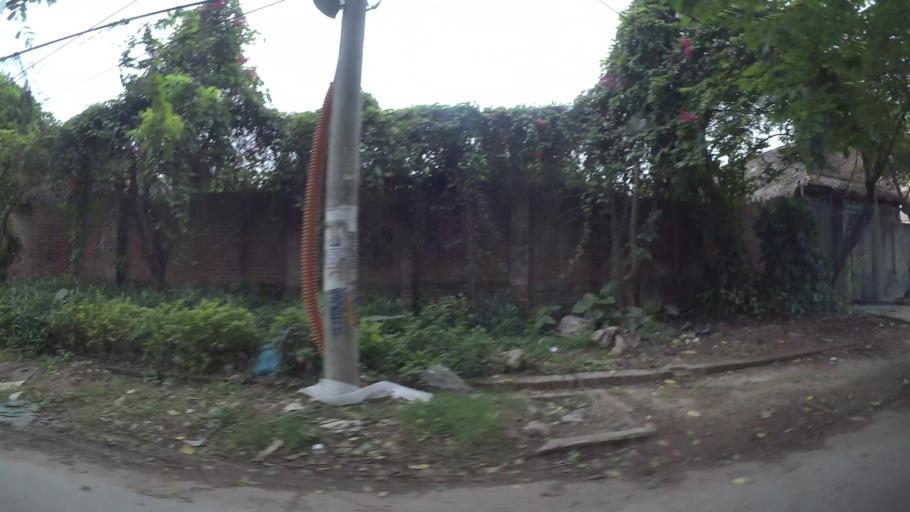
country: VN
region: Ha Noi
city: Tay Ho
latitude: 21.0602
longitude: 105.8386
